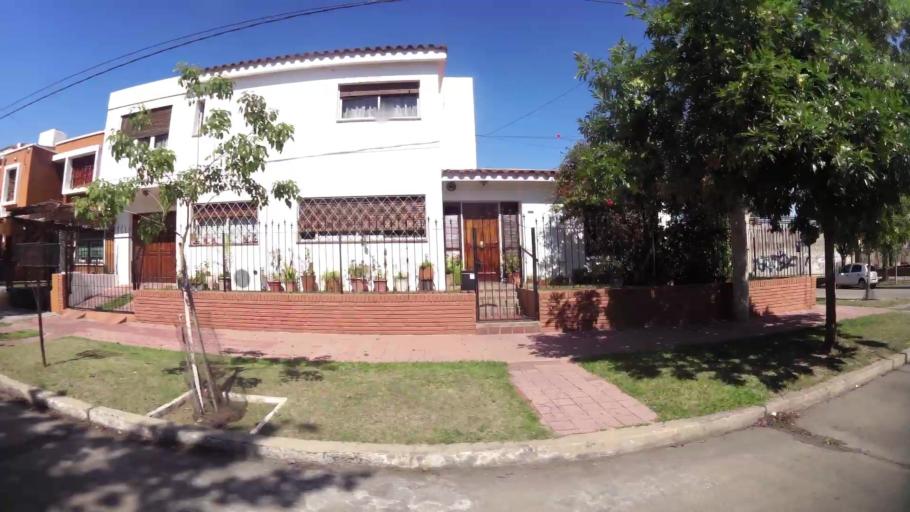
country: AR
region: Cordoba
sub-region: Departamento de Capital
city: Cordoba
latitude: -31.4206
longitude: -64.1595
